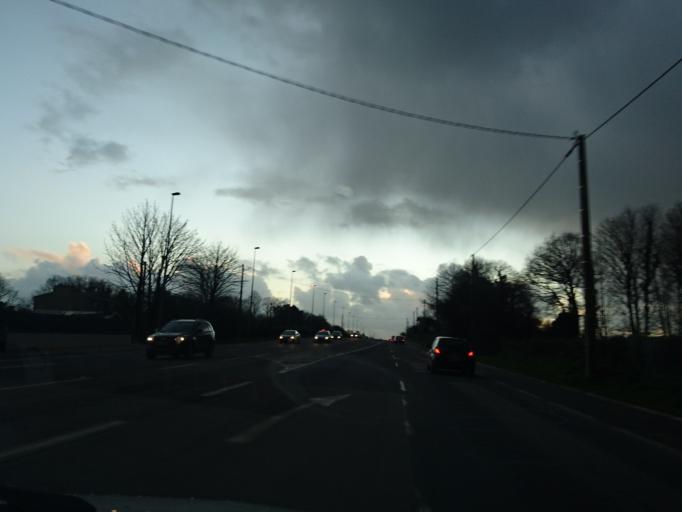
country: FR
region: Brittany
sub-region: Departement du Finistere
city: Guipavas
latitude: 48.4248
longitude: -4.4183
